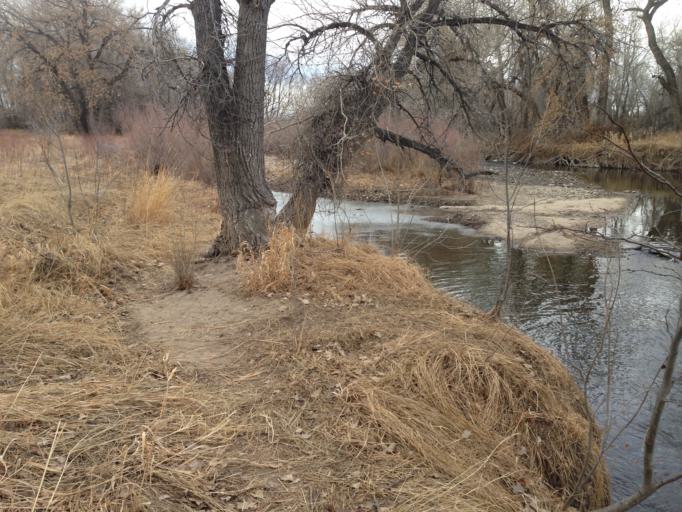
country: US
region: Colorado
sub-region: Larimer County
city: Fort Collins
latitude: 40.5356
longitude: -104.9978
